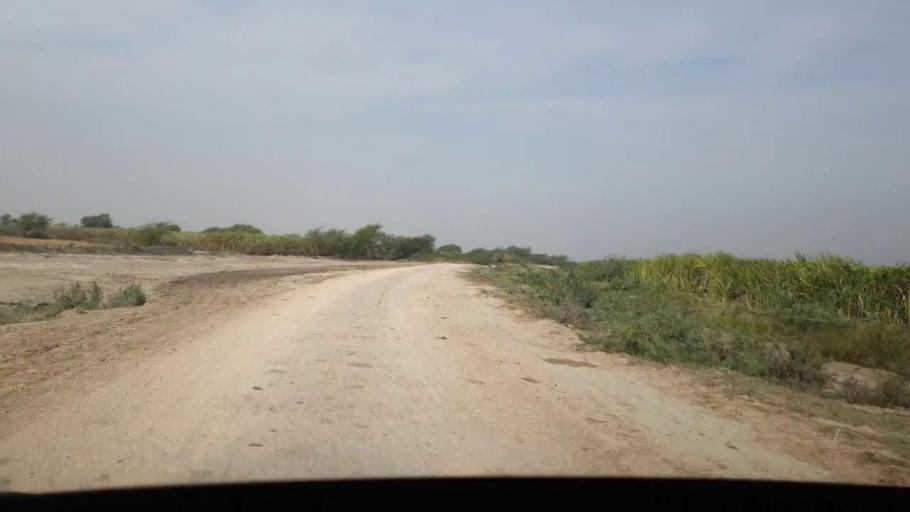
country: PK
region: Sindh
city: Chuhar Jamali
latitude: 24.3196
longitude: 67.9488
